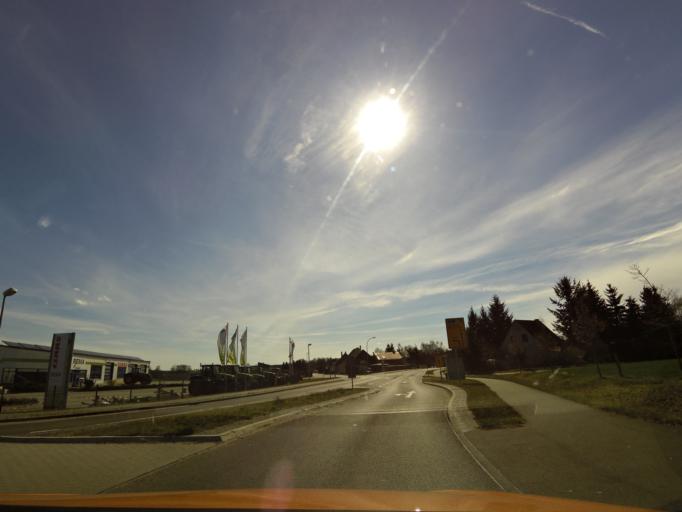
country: DE
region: Brandenburg
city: Belzig
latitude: 52.1803
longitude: 12.6238
